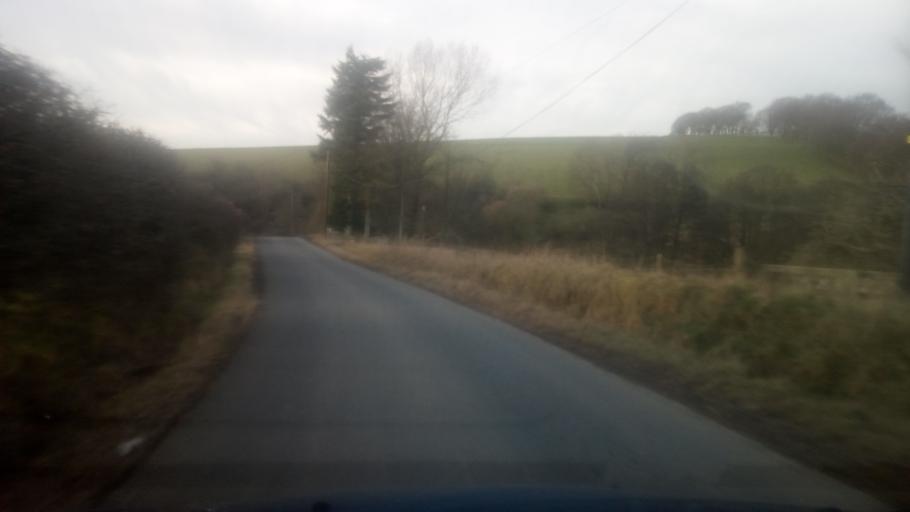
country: GB
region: Scotland
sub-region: The Scottish Borders
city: Jedburgh
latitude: 55.4086
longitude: -2.6009
